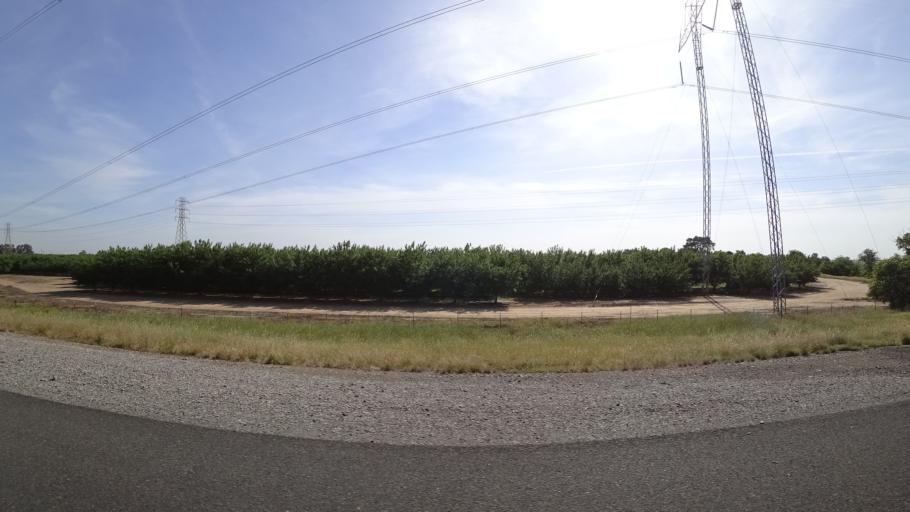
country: US
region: California
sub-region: Butte County
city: Thermalito
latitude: 39.6073
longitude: -121.6721
